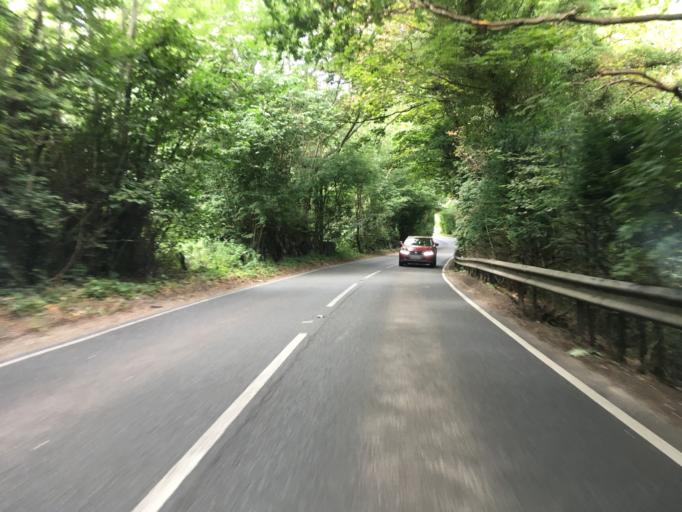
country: GB
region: England
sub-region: East Sussex
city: Crowborough
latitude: 51.1225
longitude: 0.1938
